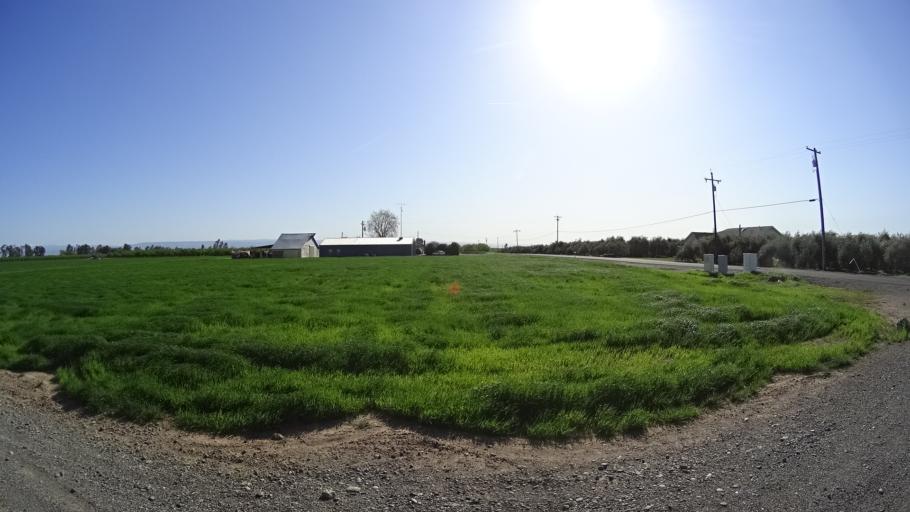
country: US
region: California
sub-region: Glenn County
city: Orland
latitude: 39.7899
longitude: -122.1041
